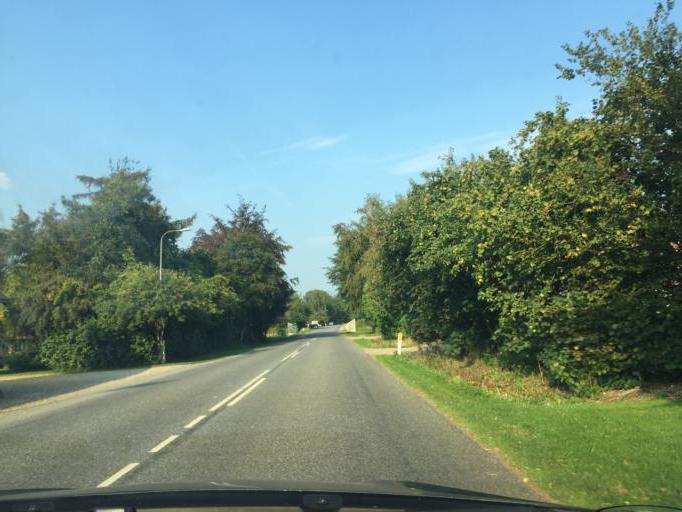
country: DK
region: South Denmark
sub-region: Faaborg-Midtfyn Kommune
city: Arslev
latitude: 55.2846
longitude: 10.5278
